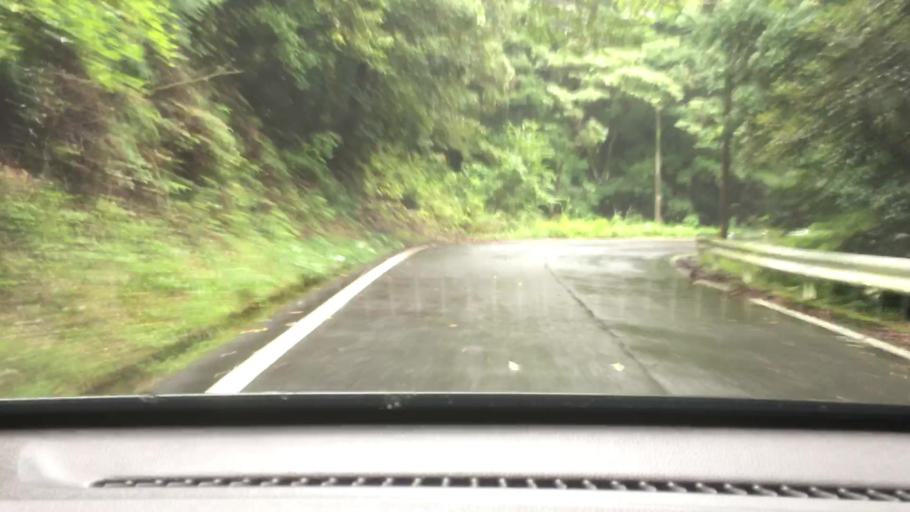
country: JP
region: Nagasaki
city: Togitsu
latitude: 32.9545
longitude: 129.7365
